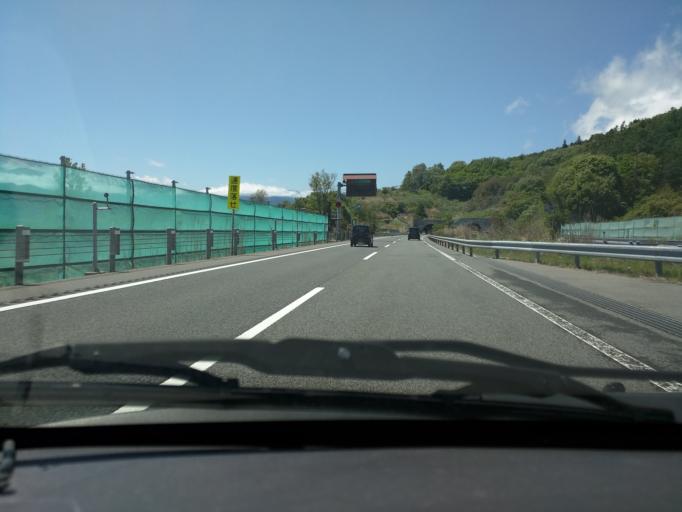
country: JP
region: Nagano
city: Nakano
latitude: 36.7563
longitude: 138.3142
